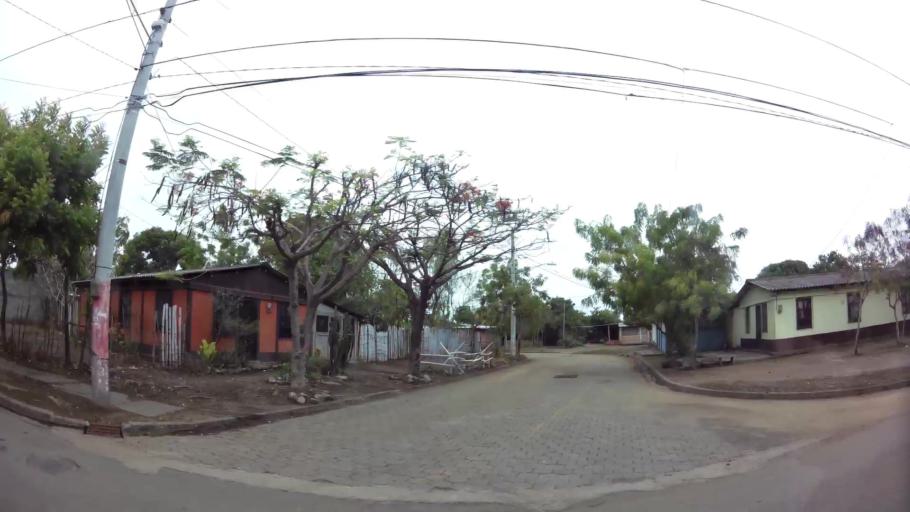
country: NI
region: Granada
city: Granada
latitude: 11.9474
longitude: -85.9468
